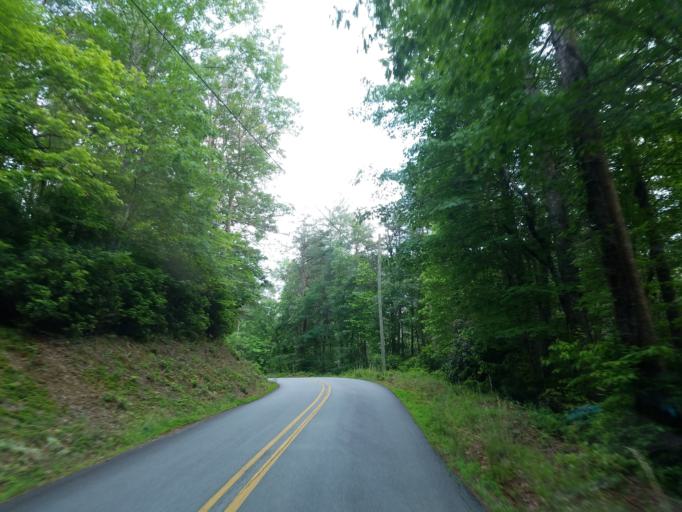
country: US
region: Georgia
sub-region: Lumpkin County
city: Dahlonega
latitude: 34.5973
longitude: -84.0731
